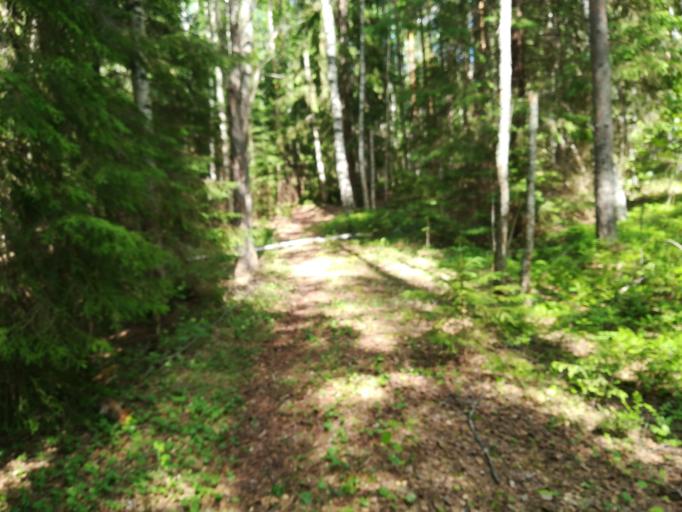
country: FI
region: South Karelia
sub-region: Imatra
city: Ruokolahti
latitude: 61.4811
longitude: 28.8697
